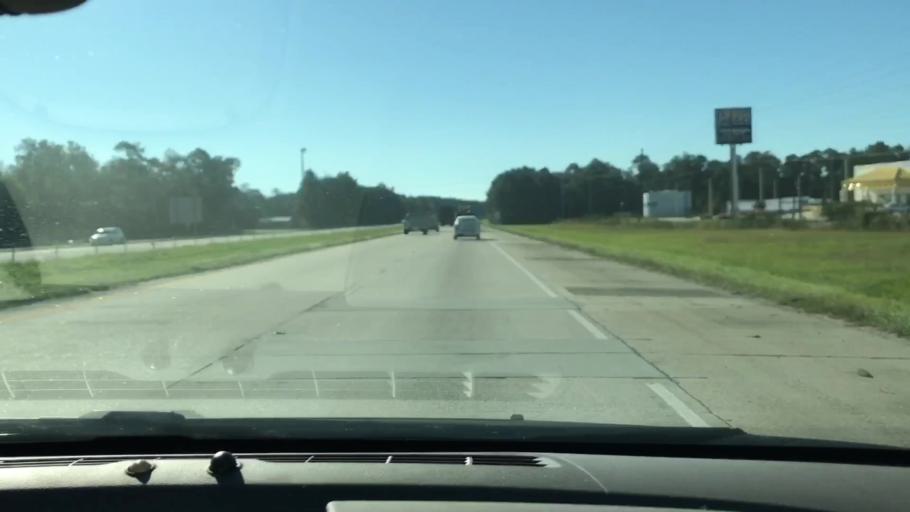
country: US
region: Louisiana
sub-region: Saint Tammany Parish
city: Pearl River
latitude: 30.3461
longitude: -89.7394
